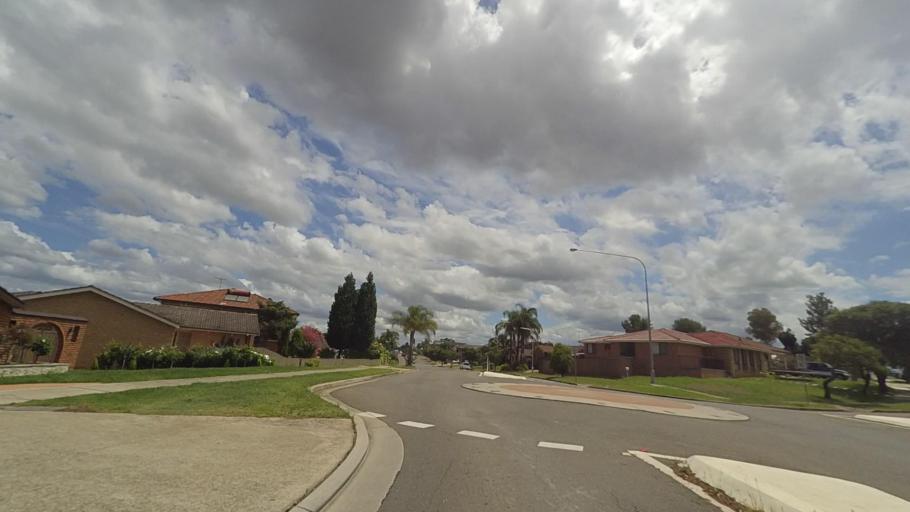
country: AU
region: New South Wales
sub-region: Fairfield
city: Cabramatta West
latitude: -33.8738
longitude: 150.9093
